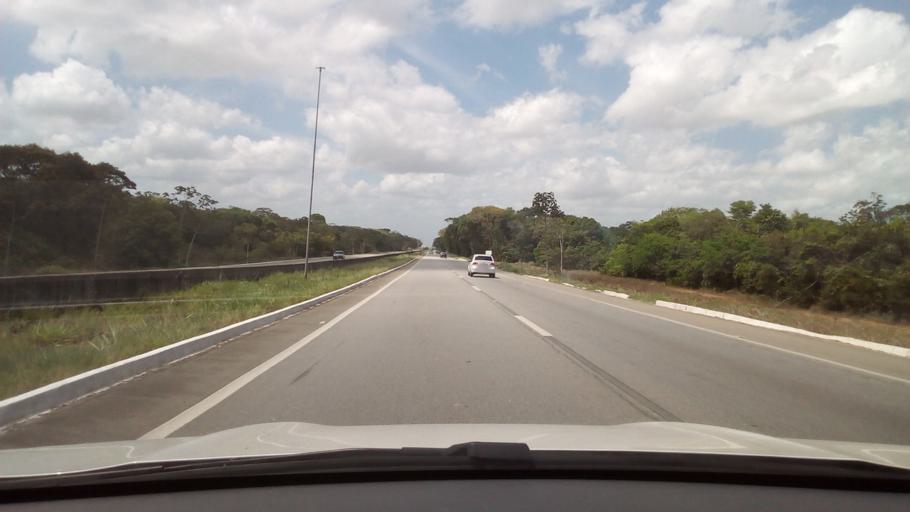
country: BR
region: Paraiba
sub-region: Cruz Do Espirito Santo
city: Cruz do Espirito Santo
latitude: -6.9853
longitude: -35.0736
